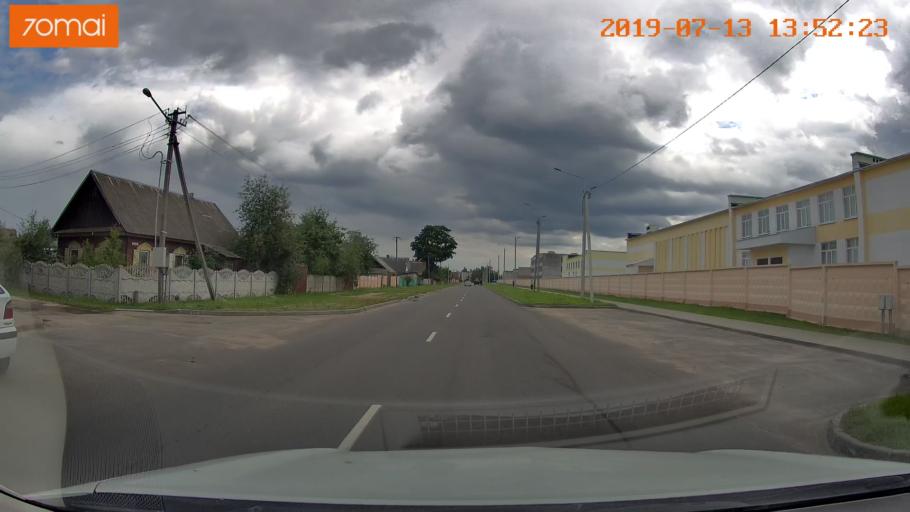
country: BY
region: Mogilev
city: Asipovichy
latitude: 53.2942
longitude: 28.6409
